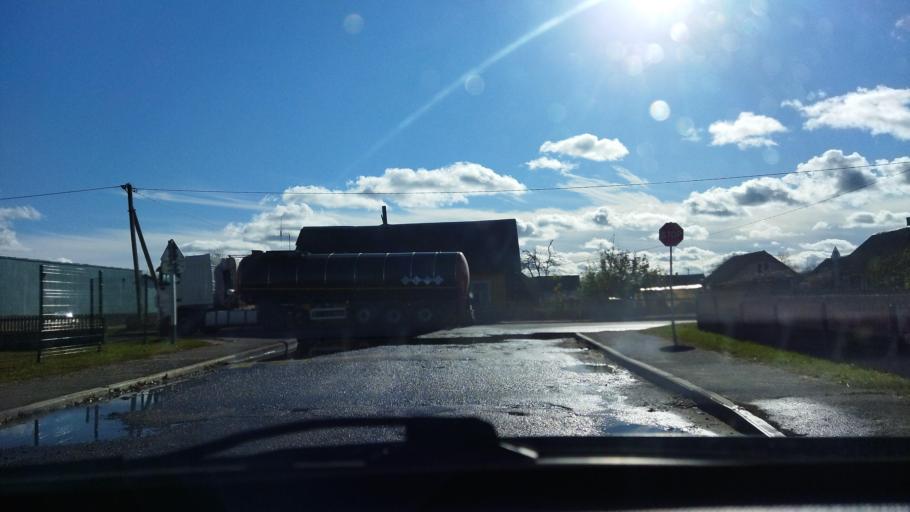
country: BY
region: Minsk
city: Svir
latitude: 54.8130
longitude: 26.1574
